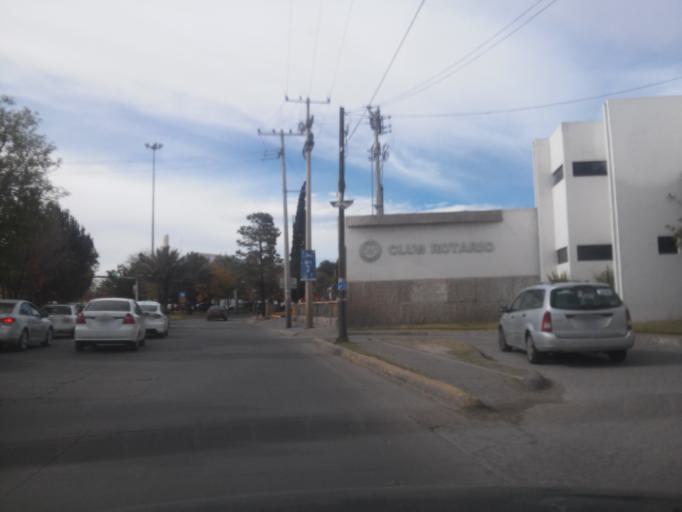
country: MX
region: Durango
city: Victoria de Durango
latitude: 24.0090
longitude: -104.6612
